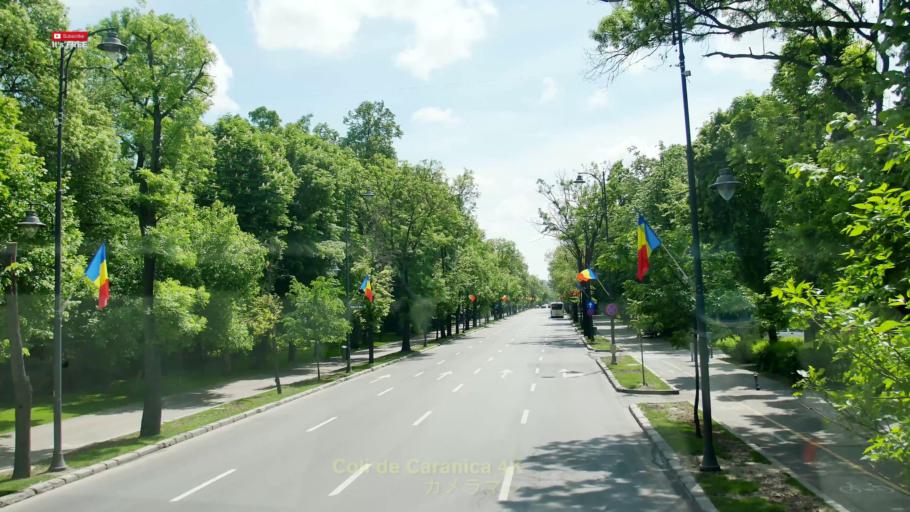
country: RO
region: Bucuresti
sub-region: Municipiul Bucuresti
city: Bucuresti
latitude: 44.4657
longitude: 26.0787
